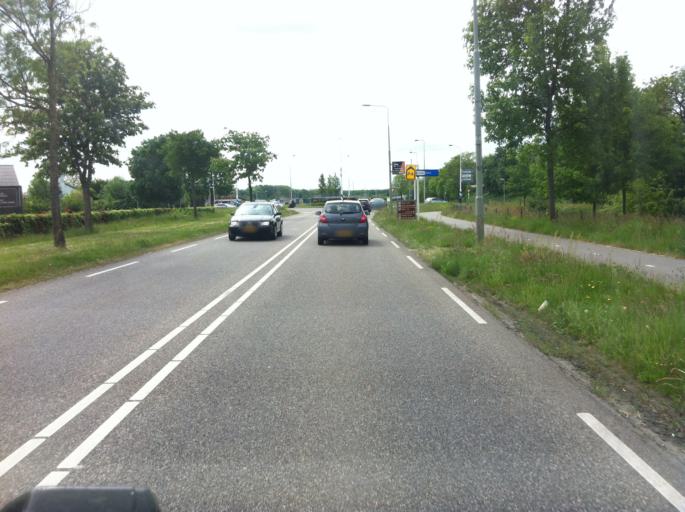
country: NL
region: Limburg
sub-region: Gemeente Roermond
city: Leeuwen
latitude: 51.1944
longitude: 6.0278
